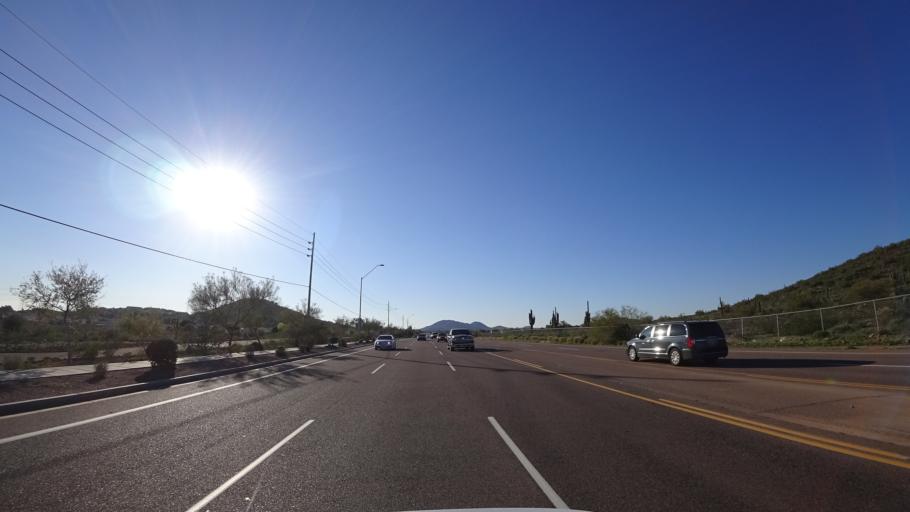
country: US
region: Arizona
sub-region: Maricopa County
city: Peoria
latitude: 33.7123
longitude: -112.1889
